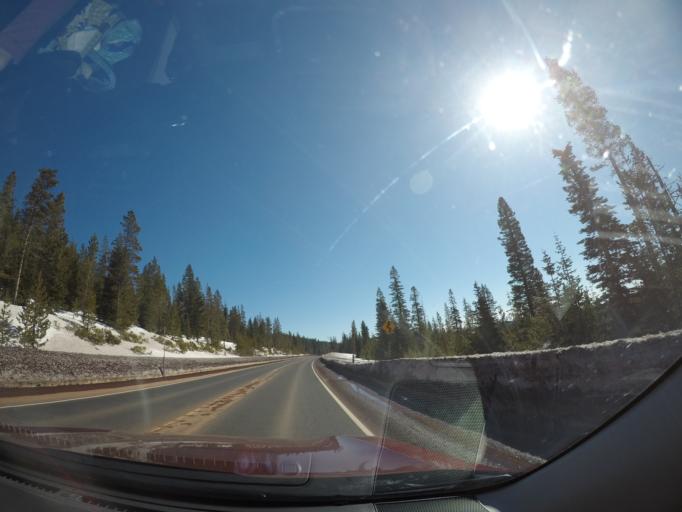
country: US
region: Oregon
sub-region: Deschutes County
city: Sunriver
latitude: 43.9837
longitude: -121.6005
